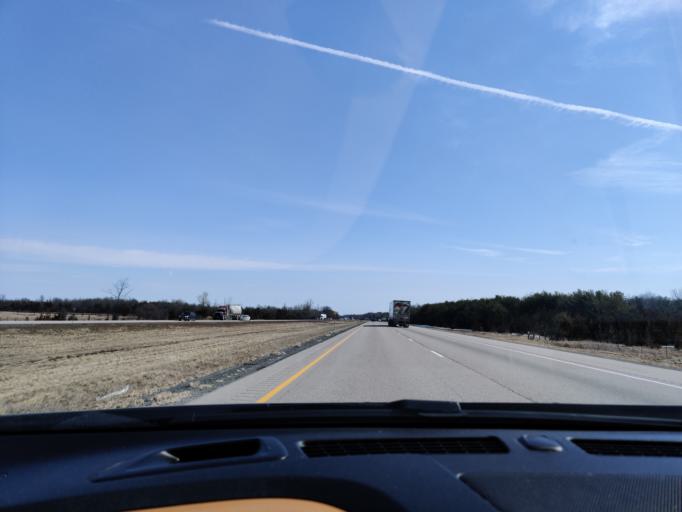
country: CA
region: Ontario
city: Skatepark
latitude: 44.2726
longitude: -76.9051
